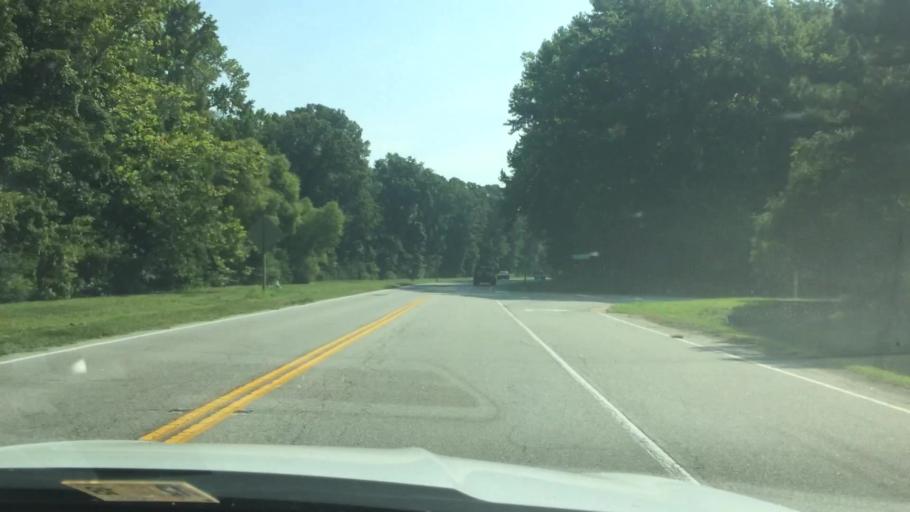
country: US
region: Virginia
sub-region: City of Poquoson
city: Poquoson
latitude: 37.1253
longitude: -76.4072
